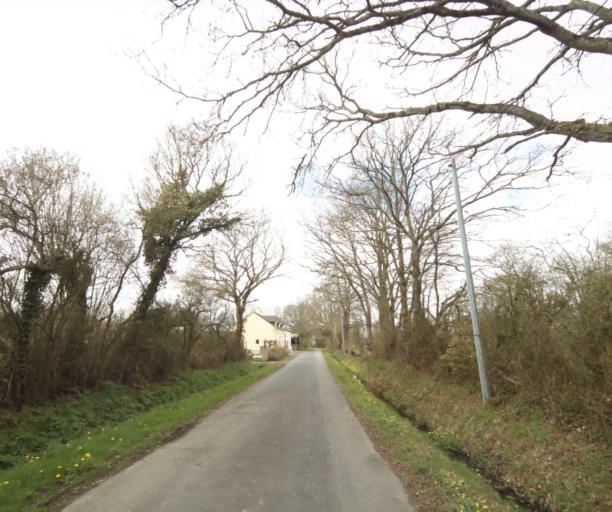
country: FR
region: Pays de la Loire
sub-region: Departement de la Loire-Atlantique
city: Bouvron
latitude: 47.4379
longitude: -1.8554
